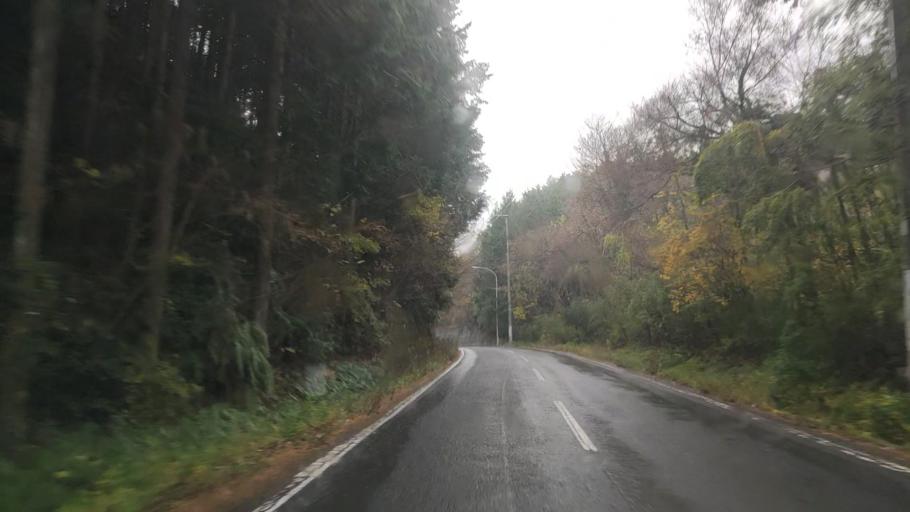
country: JP
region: Tokushima
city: Kamojimacho-jogejima
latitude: 34.2102
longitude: 134.3516
